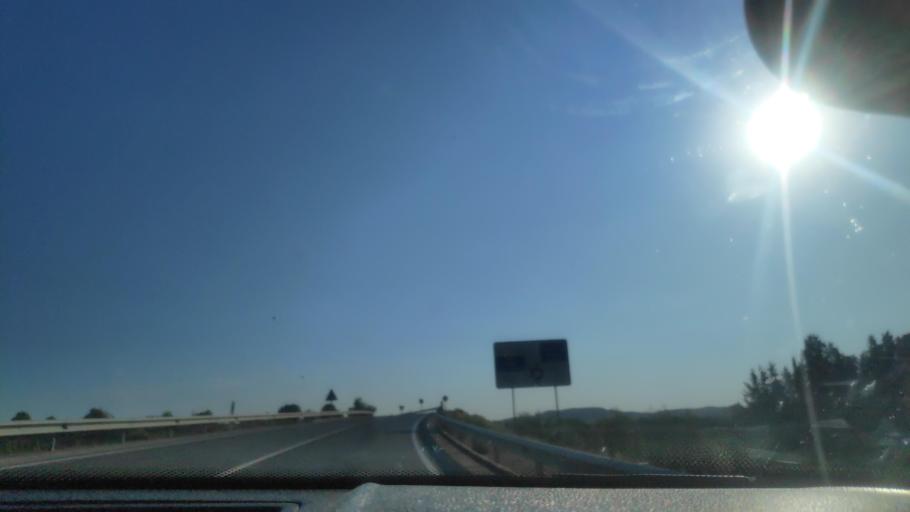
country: ES
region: Andalusia
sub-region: Provincia de Jaen
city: La Guardia de Jaen
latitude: 37.8000
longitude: -3.7193
